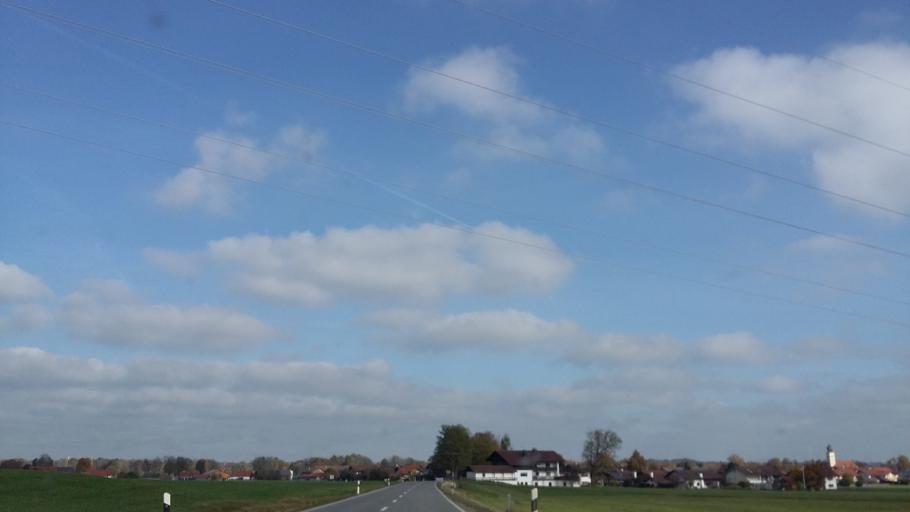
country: DE
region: Bavaria
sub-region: Upper Bavaria
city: Bruckmuhl
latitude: 47.8588
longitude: 11.9354
